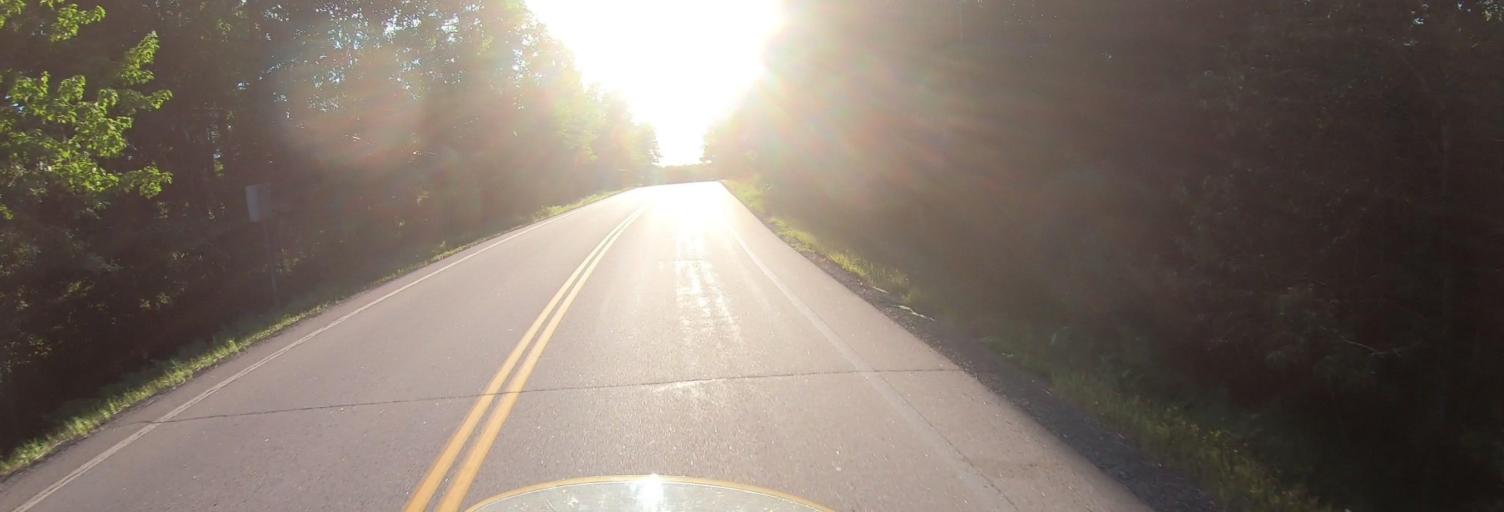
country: US
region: Minnesota
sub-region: Saint Louis County
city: Ely
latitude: 47.9277
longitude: -91.7643
